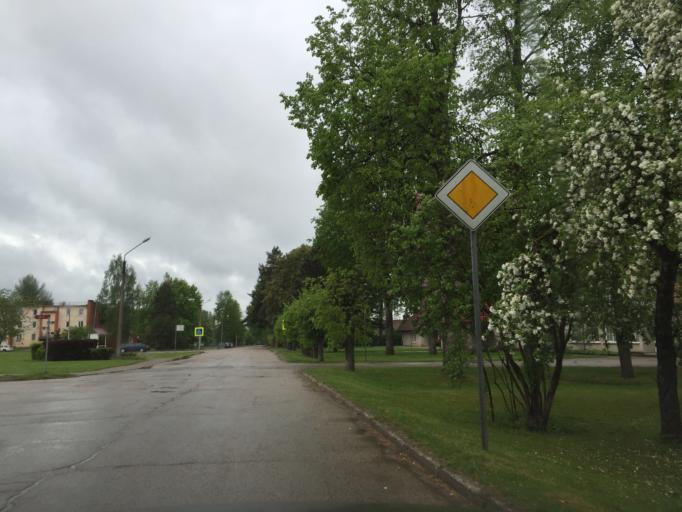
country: LV
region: Ogre
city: Jumprava
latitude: 56.6766
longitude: 24.9728
